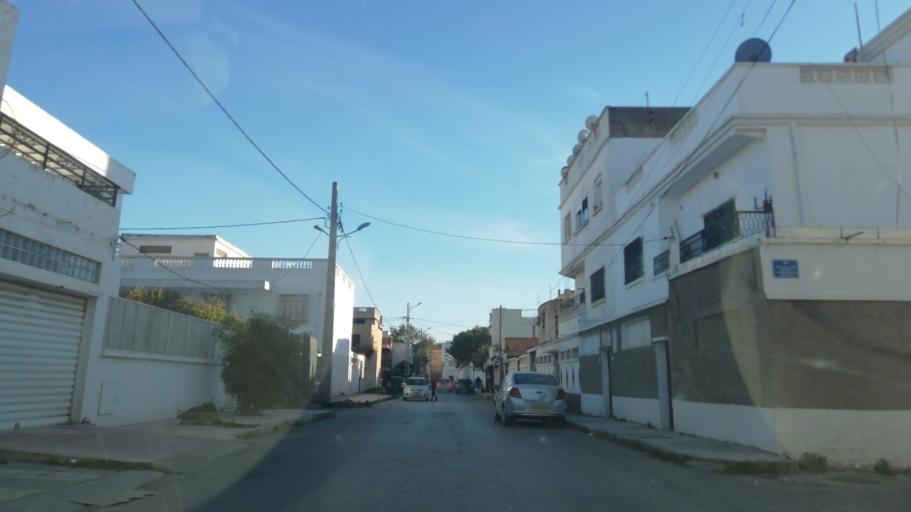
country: DZ
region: Oran
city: Oran
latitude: 35.7092
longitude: -0.6073
